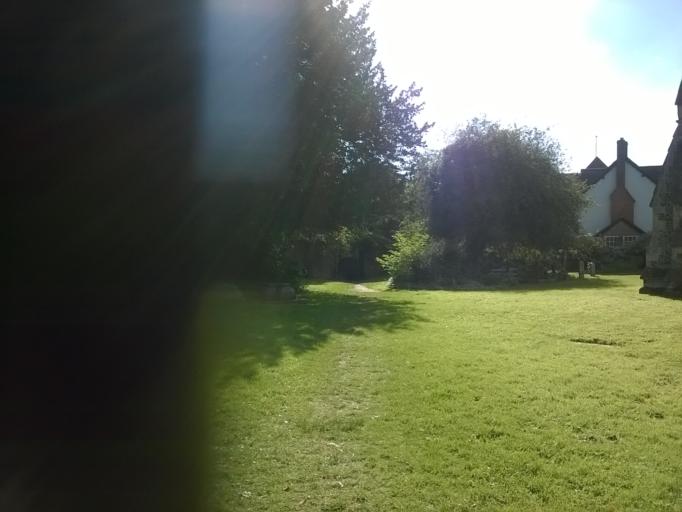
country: GB
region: England
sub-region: West Berkshire
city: Pangbourne
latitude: 51.4883
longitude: -1.0867
